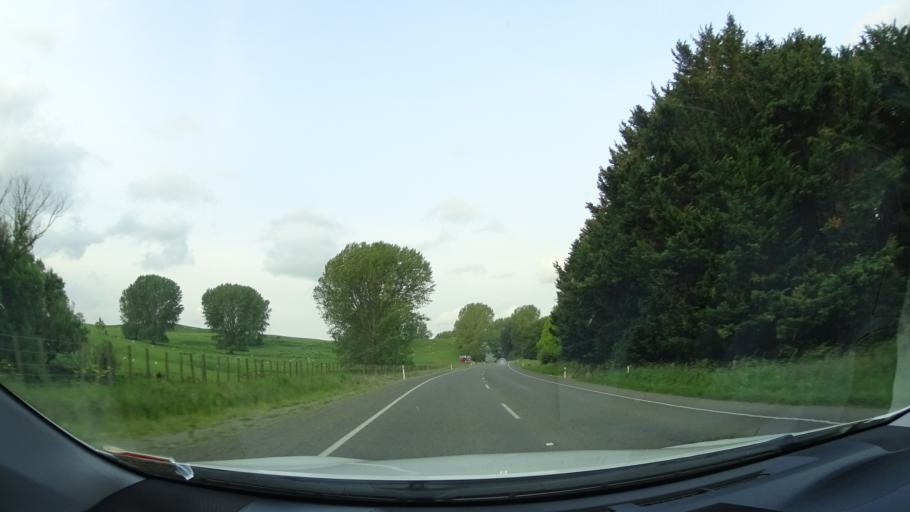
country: NZ
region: Manawatu-Wanganui
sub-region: Ruapehu District
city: Waiouru
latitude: -39.7421
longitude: 175.8365
